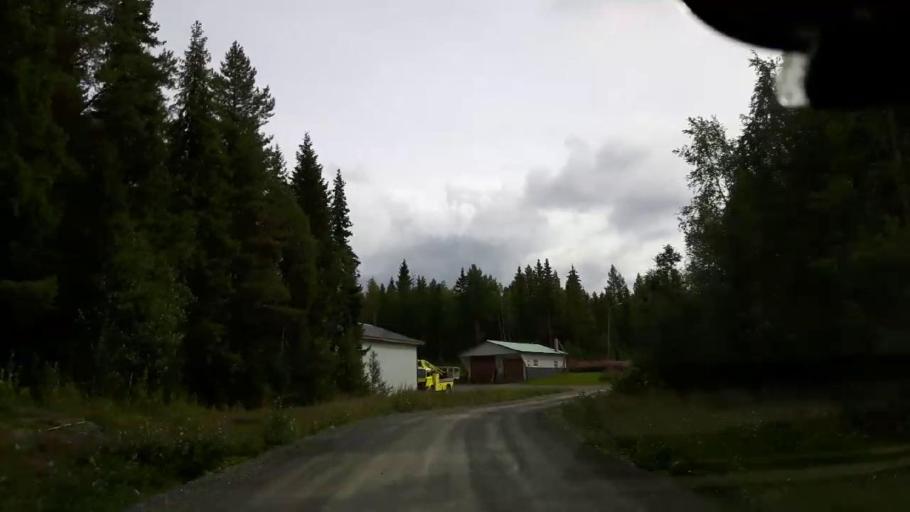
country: SE
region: Jaemtland
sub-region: Krokoms Kommun
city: Valla
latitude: 63.6371
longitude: 14.0144
